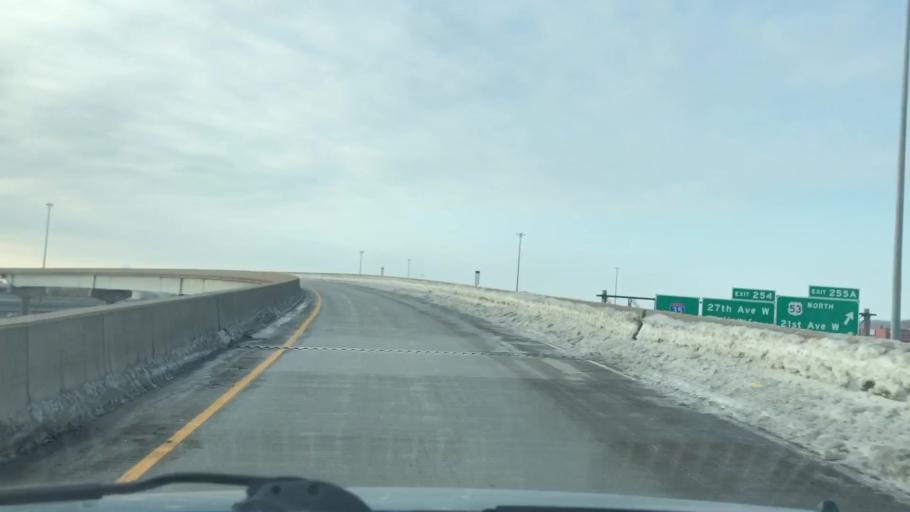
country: US
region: Minnesota
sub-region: Saint Louis County
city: Duluth
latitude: 46.7677
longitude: -92.1204
